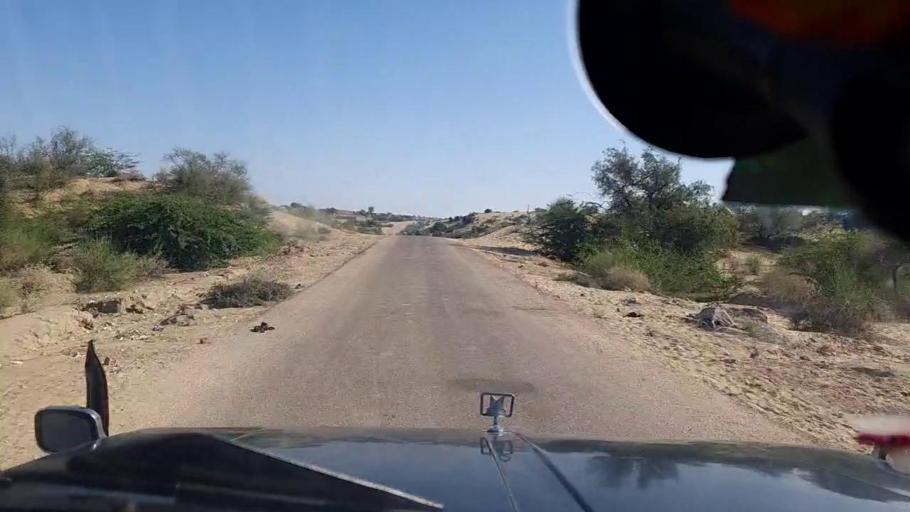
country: PK
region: Sindh
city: Diplo
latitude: 24.4758
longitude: 69.7921
